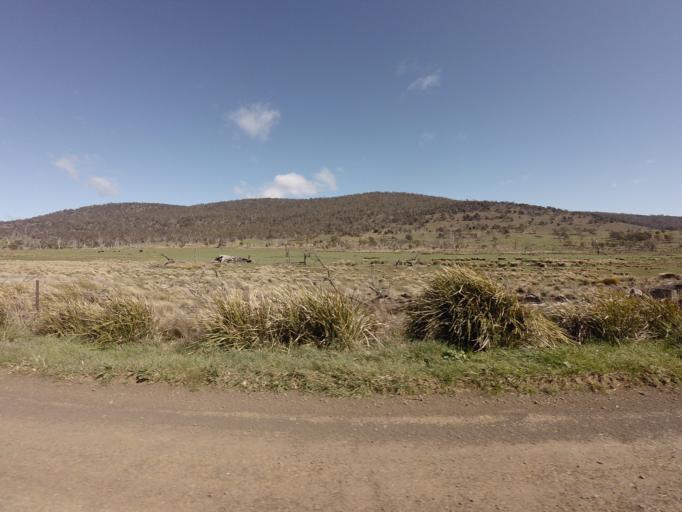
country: AU
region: Tasmania
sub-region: Northern Midlands
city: Evandale
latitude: -41.9340
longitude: 147.4183
